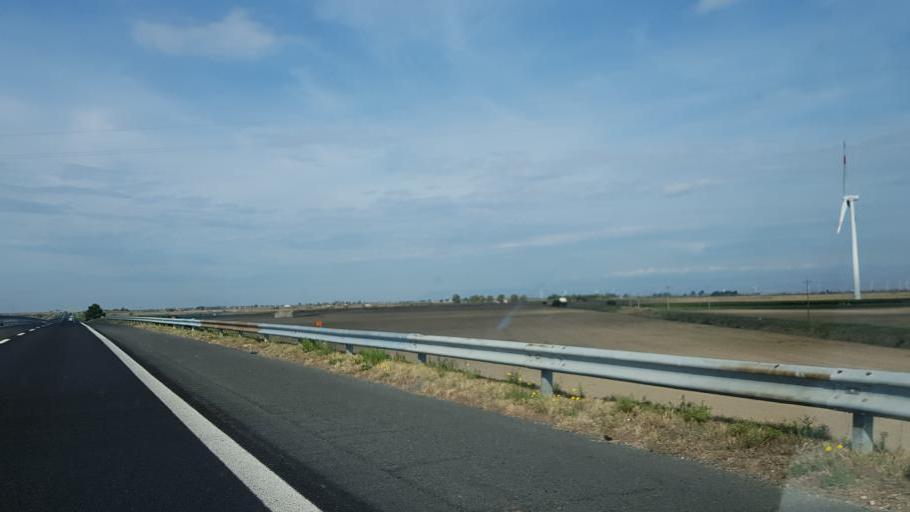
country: IT
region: Apulia
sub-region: Provincia di Foggia
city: Orta Nova
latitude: 41.3726
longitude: 15.7674
